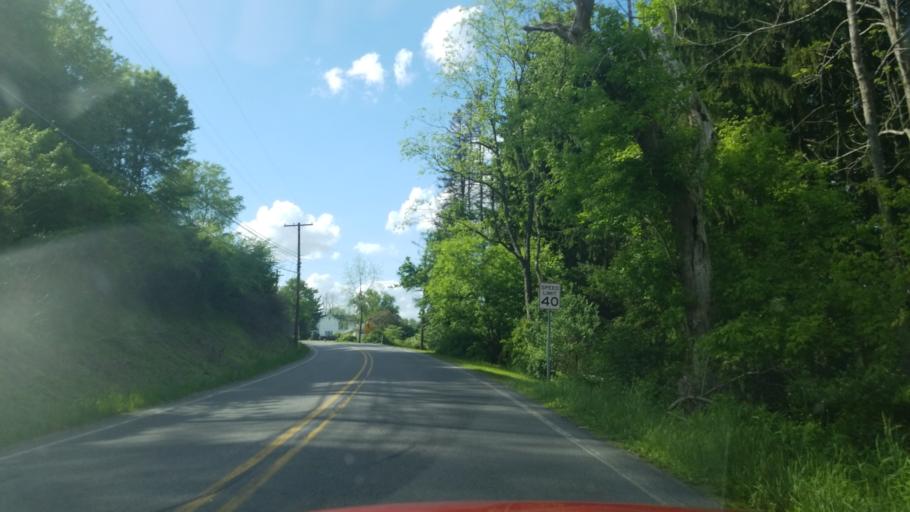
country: US
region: Pennsylvania
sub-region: Centre County
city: Philipsburg
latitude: 40.9116
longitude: -78.2476
